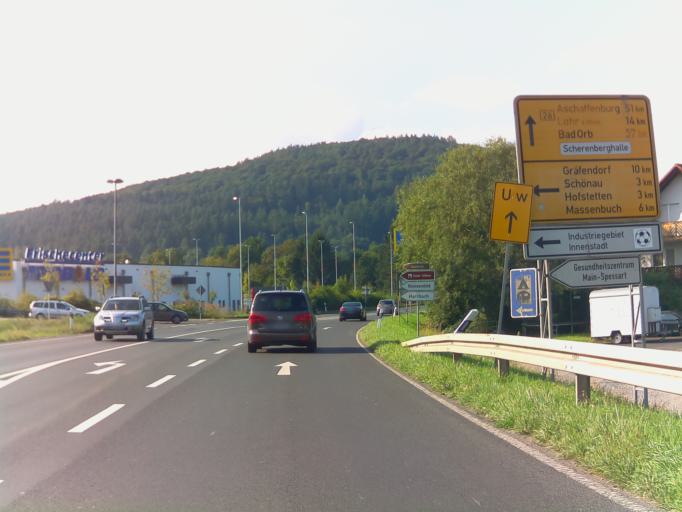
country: DE
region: Bavaria
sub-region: Regierungsbezirk Unterfranken
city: Gemunden
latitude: 50.0579
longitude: 9.6857
